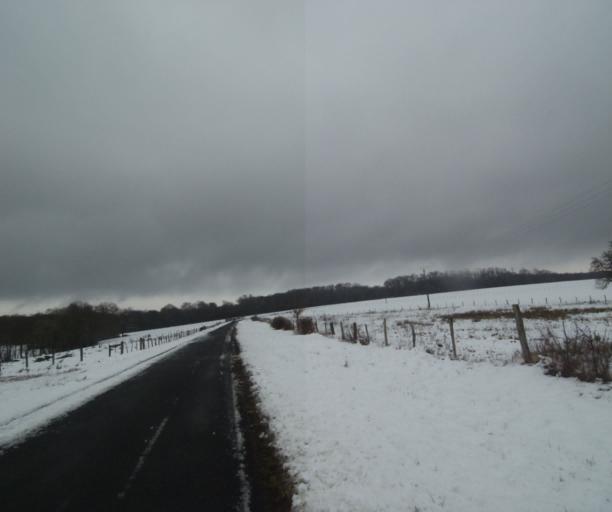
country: FR
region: Champagne-Ardenne
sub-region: Departement de la Haute-Marne
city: Laneuville-a-Remy
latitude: 48.5114
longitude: 4.8832
